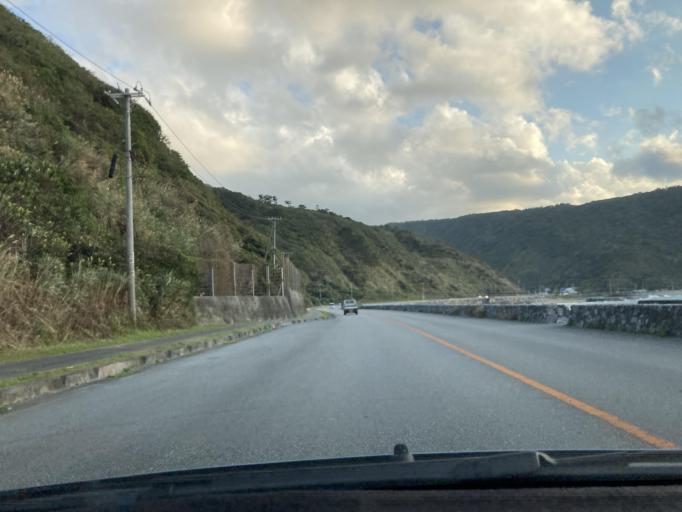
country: JP
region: Okinawa
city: Nago
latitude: 26.7720
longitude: 128.2047
